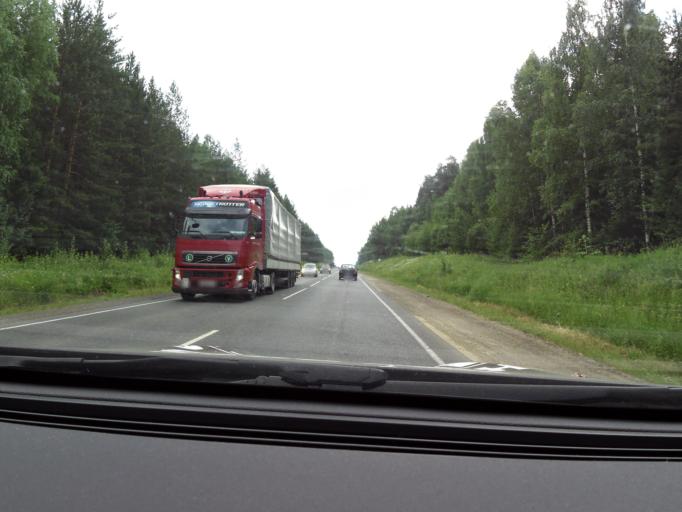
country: RU
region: Perm
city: Kungur
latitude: 57.4459
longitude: 56.8127
